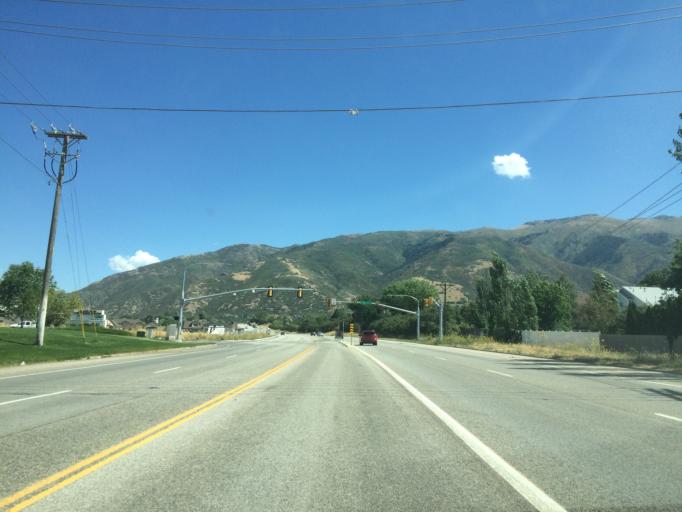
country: US
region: Utah
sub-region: Davis County
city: South Weber
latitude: 41.1016
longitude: -111.9340
